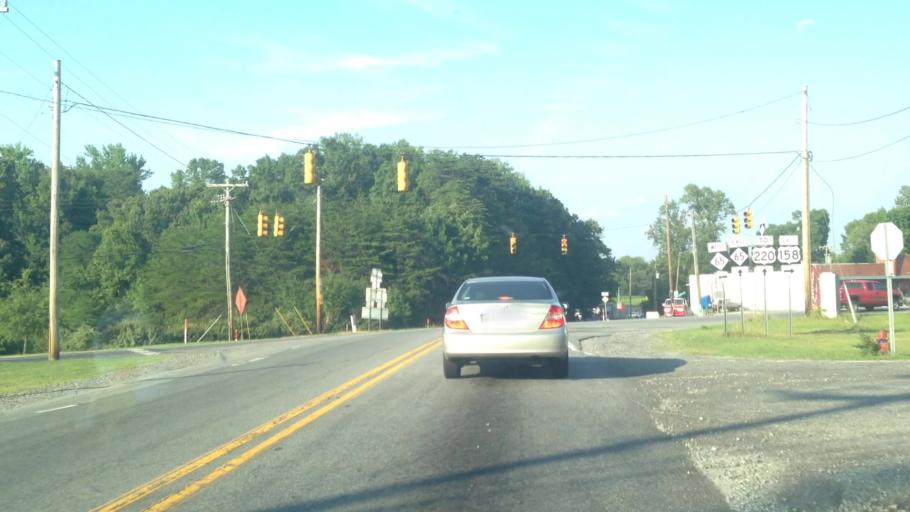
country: US
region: North Carolina
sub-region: Guilford County
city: Stokesdale
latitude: 36.2447
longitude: -79.9902
